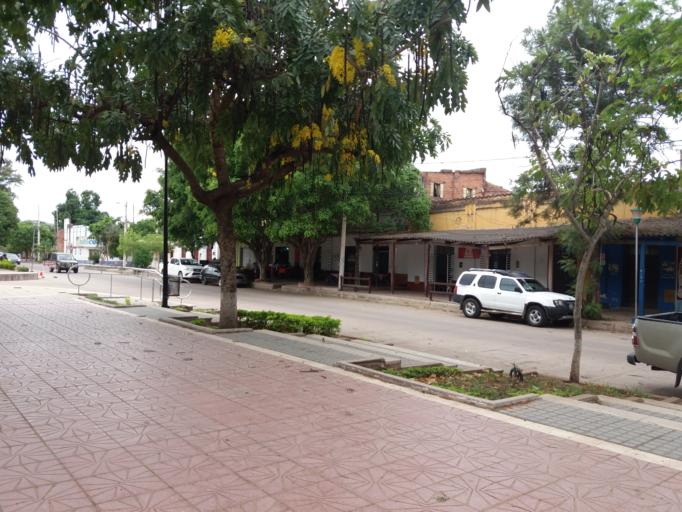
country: BO
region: Tarija
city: Villamontes
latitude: -21.2647
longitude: -63.4734
